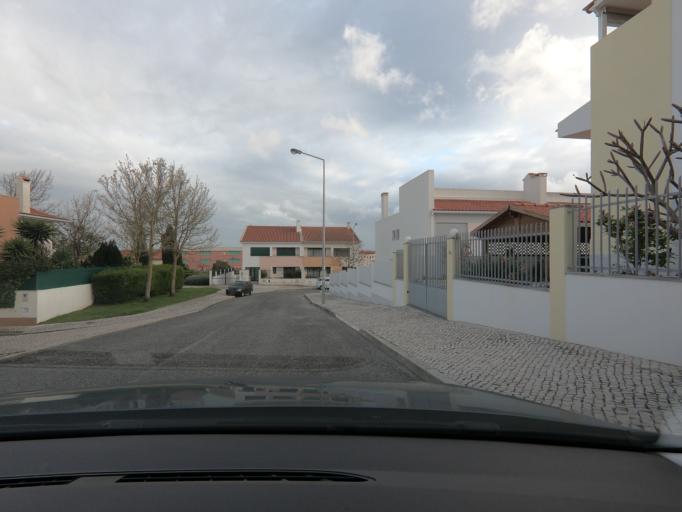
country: PT
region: Lisbon
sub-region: Cascais
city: Sao Domingos de Rana
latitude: 38.7305
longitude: -9.3283
